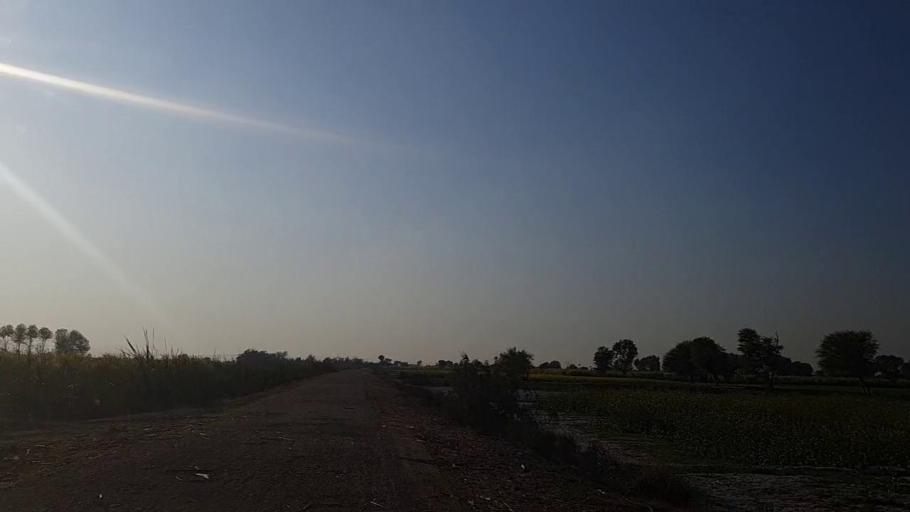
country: PK
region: Sindh
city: Sakrand
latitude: 26.3113
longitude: 68.1662
